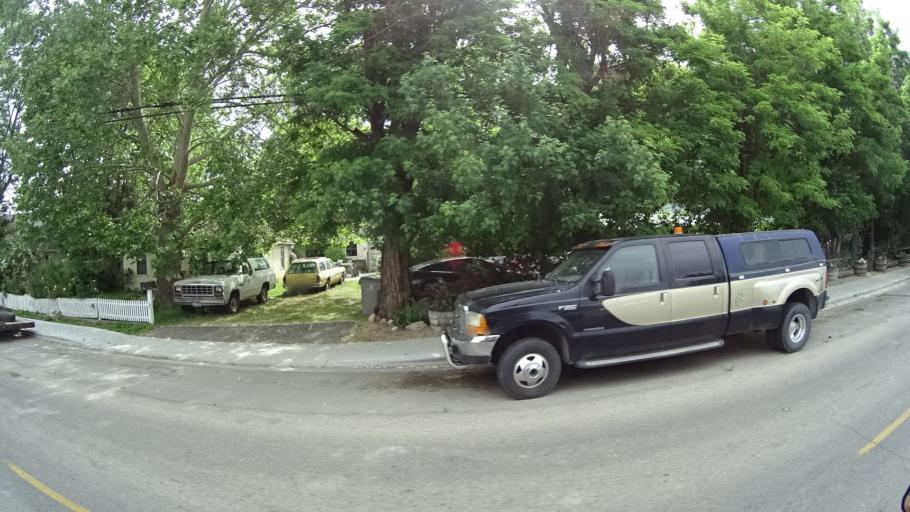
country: US
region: Idaho
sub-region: Ada County
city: Boise
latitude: 43.5814
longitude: -116.2237
